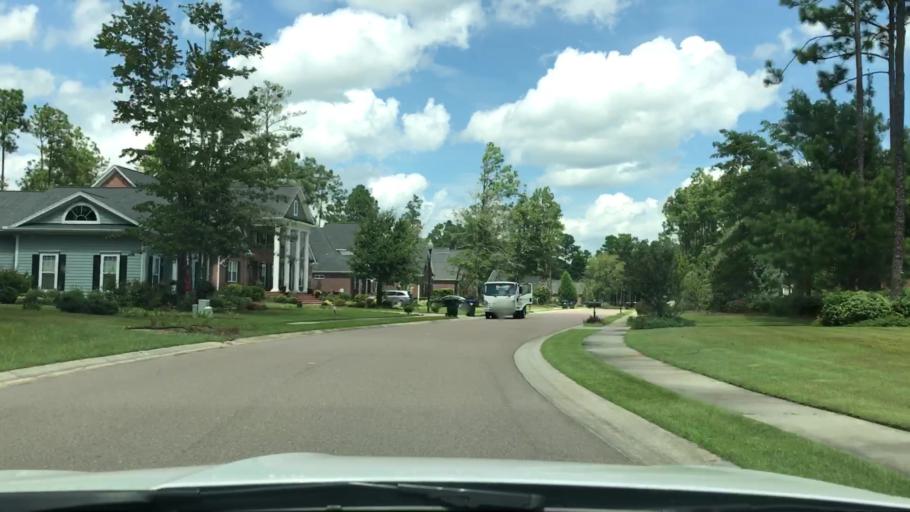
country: US
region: South Carolina
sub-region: Dorchester County
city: Summerville
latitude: 33.0350
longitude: -80.2205
